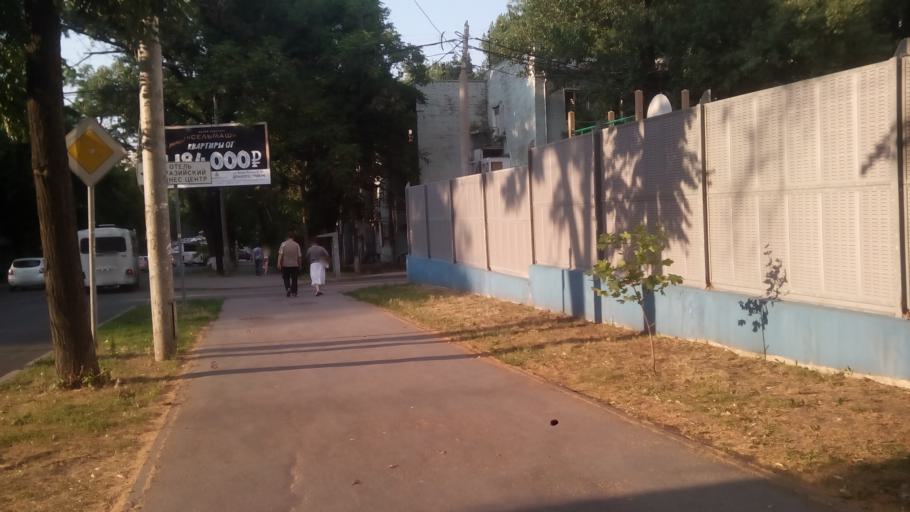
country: RU
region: Rostov
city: Imeni Chkalova
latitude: 47.2550
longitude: 39.7680
